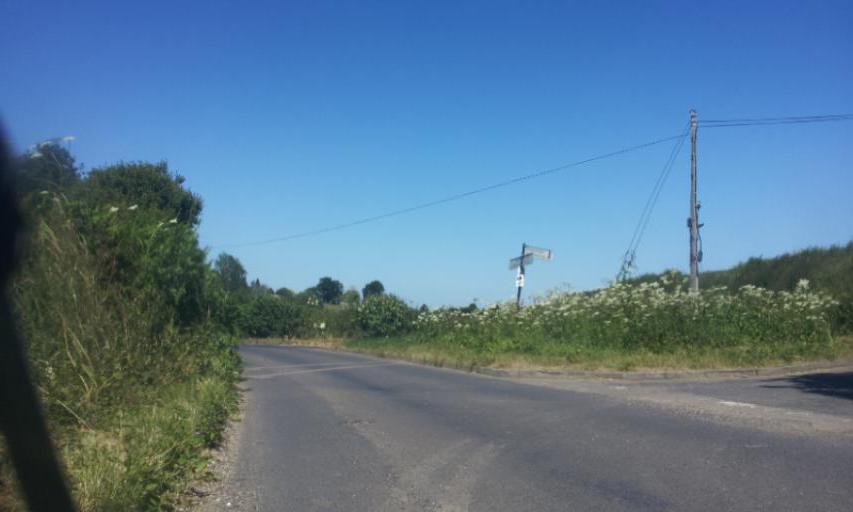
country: GB
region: England
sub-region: Kent
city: Sittingbourne
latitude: 51.3063
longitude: 0.7401
